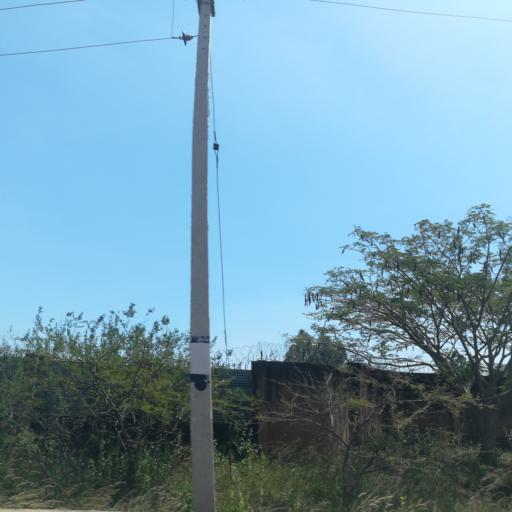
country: NG
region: Plateau
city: Bukuru
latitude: 9.8173
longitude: 8.8752
